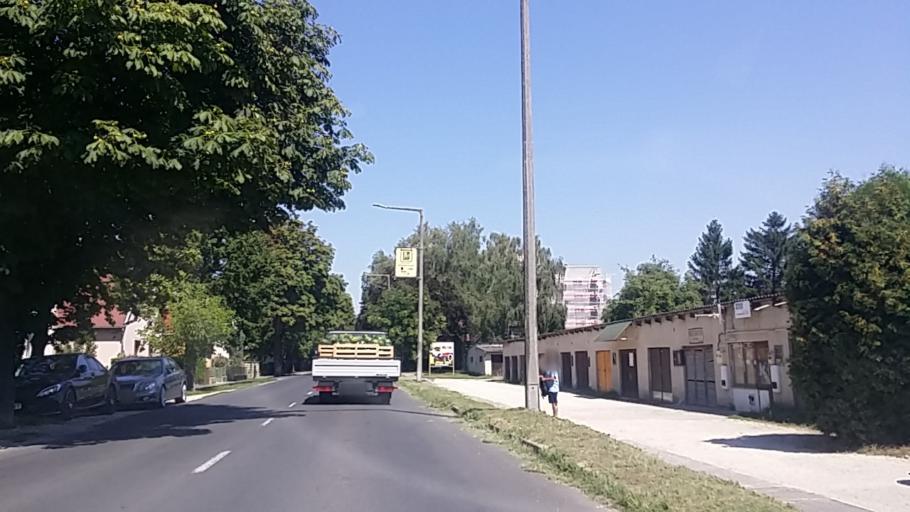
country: HU
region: Zala
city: Keszthely
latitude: 46.7543
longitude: 17.2393
